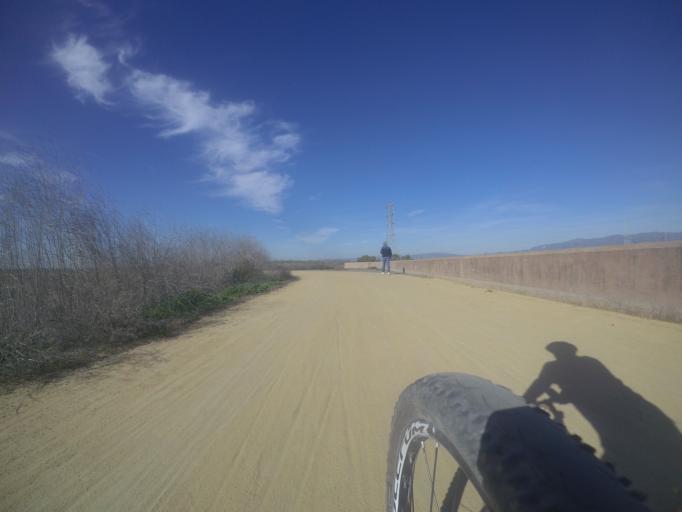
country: US
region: California
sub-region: Santa Clara County
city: Sunnyvale
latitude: 37.4164
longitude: -121.9871
